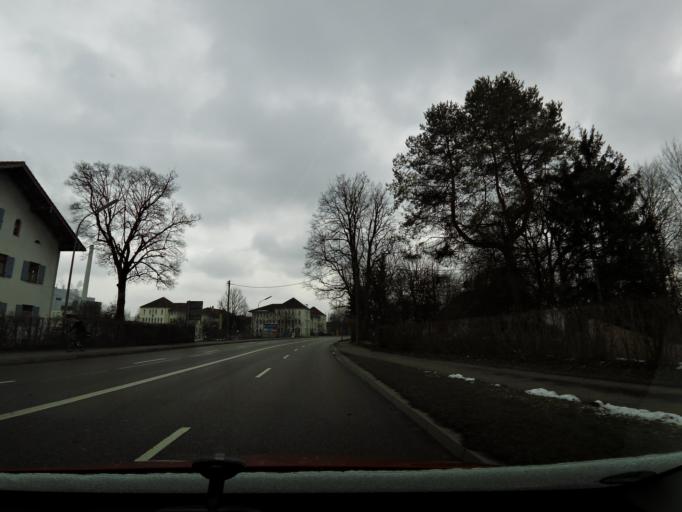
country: DE
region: Bavaria
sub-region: Upper Bavaria
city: Unterfoehring
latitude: 48.1854
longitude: 11.6340
